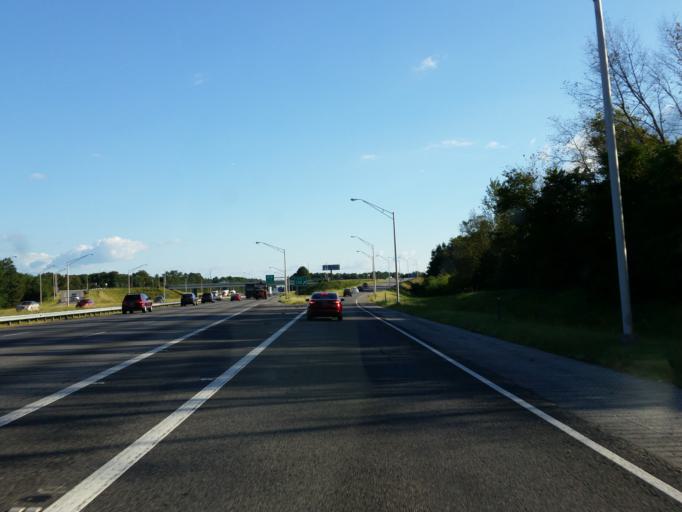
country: US
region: Georgia
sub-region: Houston County
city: Perry
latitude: 32.4971
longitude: -83.7429
